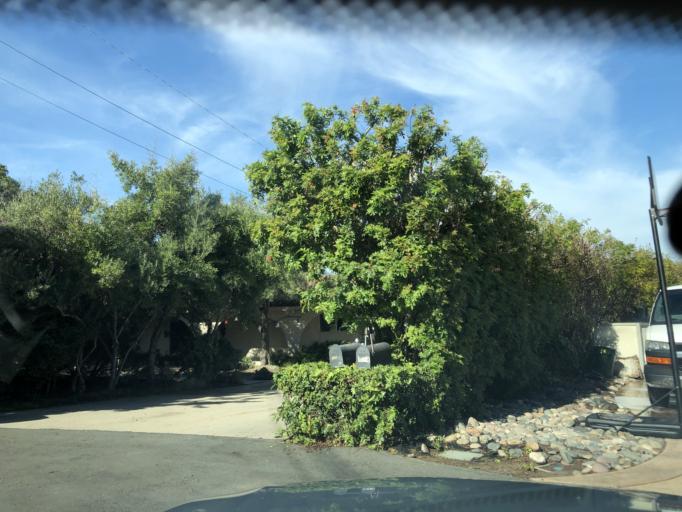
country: US
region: California
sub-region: San Diego County
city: Chula Vista
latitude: 32.6441
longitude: -117.0620
